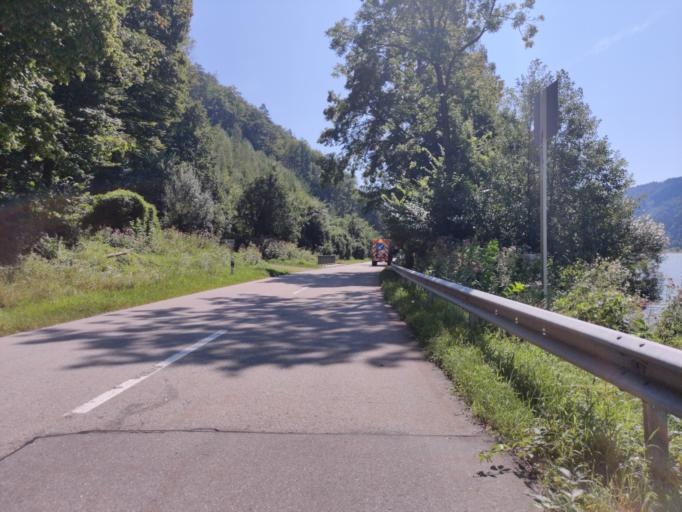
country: DE
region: Bavaria
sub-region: Lower Bavaria
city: Untergriesbach
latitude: 48.5280
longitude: 13.6898
